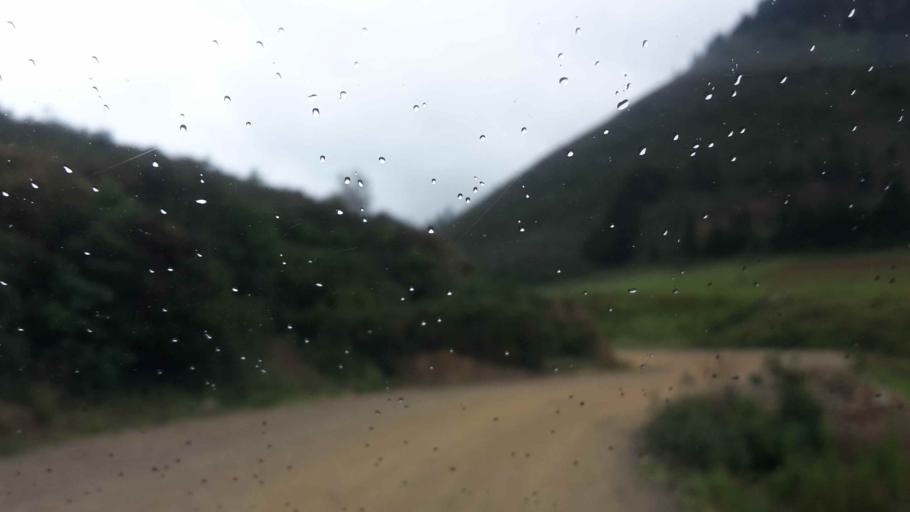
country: BO
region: Cochabamba
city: Totora
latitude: -17.5799
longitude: -65.2887
